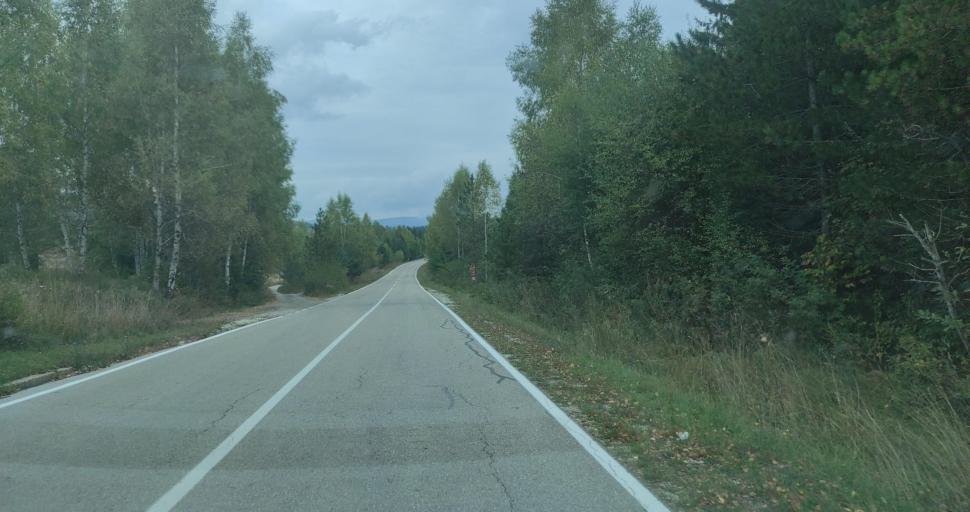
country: RS
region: Central Serbia
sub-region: Jablanicki Okrug
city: Crna Trava
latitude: 42.6885
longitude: 22.3166
